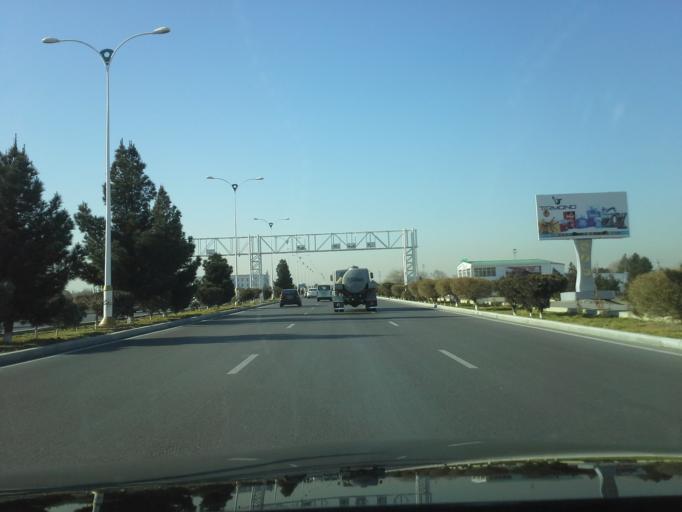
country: TM
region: Ahal
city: Annau
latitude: 37.9090
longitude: 58.5063
